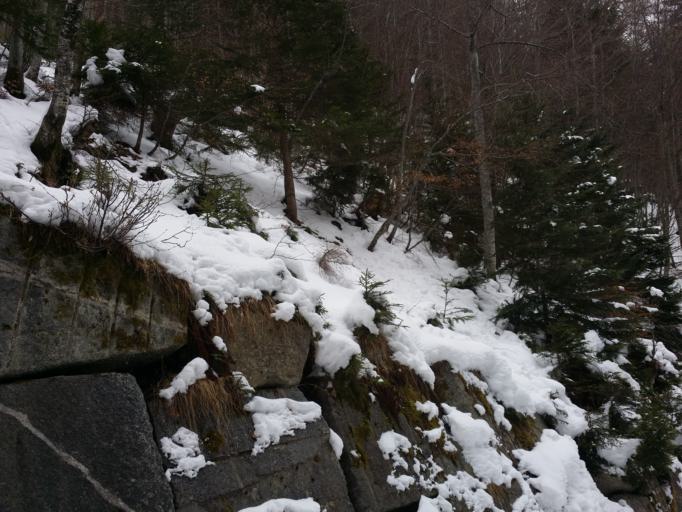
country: IT
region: Piedmont
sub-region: Provincia Verbano-Cusio-Ossola
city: Crodo
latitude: 46.2172
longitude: 8.2930
